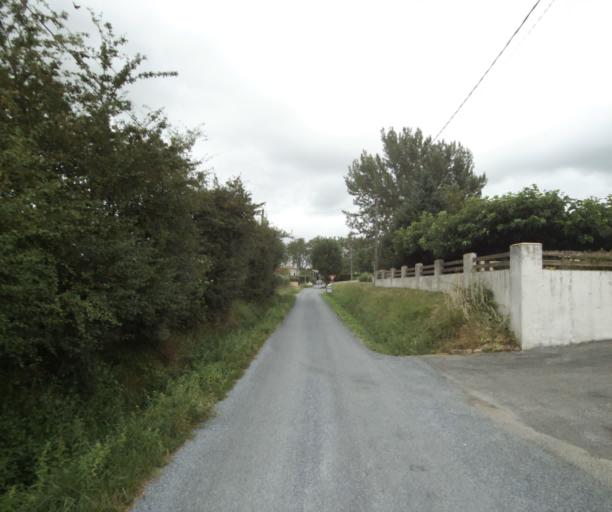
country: FR
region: Midi-Pyrenees
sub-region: Departement du Tarn
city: Soreze
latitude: 43.4486
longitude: 2.0585
